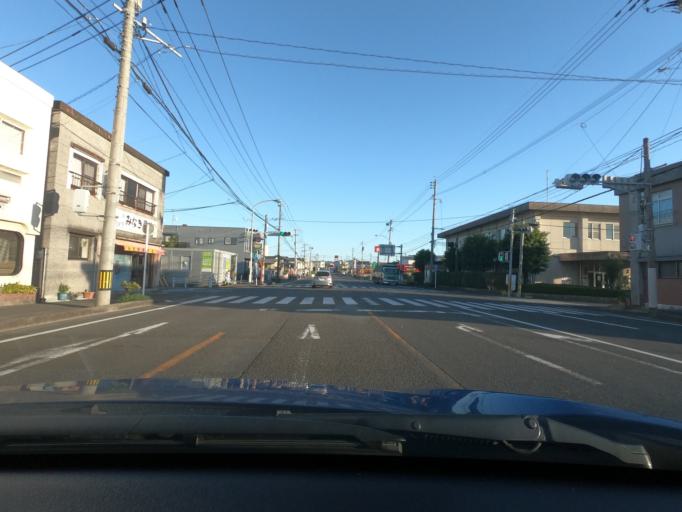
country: JP
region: Kagoshima
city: Satsumasendai
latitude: 31.8327
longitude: 130.2933
